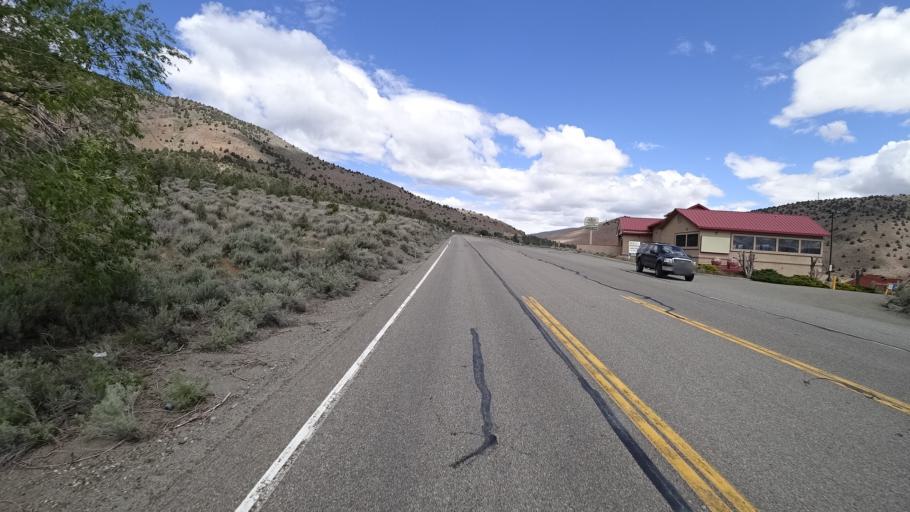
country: US
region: Nevada
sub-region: Lyon County
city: Smith Valley
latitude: 38.6983
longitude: -119.5500
